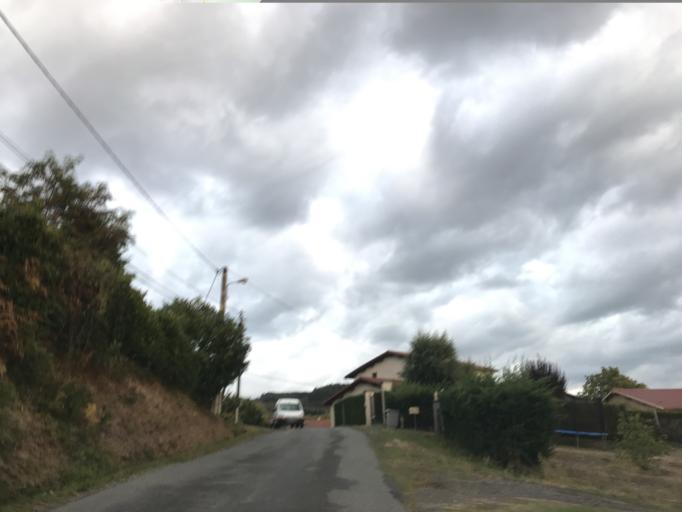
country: FR
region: Auvergne
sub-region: Departement du Puy-de-Dome
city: Escoutoux
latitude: 45.8260
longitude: 3.5628
